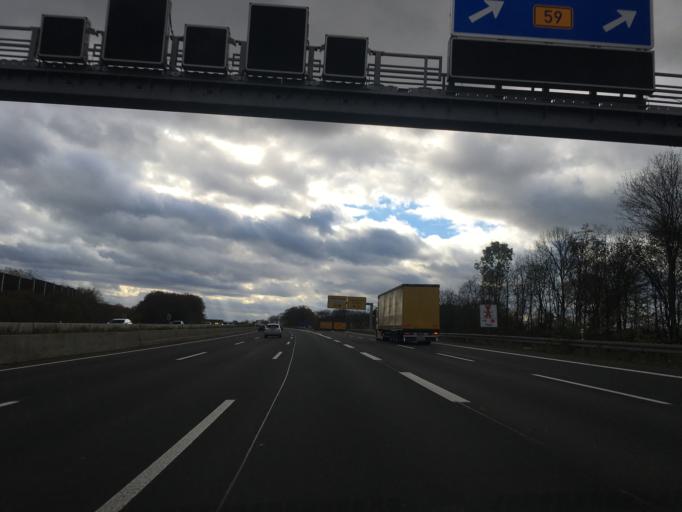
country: DE
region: North Rhine-Westphalia
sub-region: Regierungsbezirk Koln
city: Mengenich
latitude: 50.9814
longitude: 6.8530
